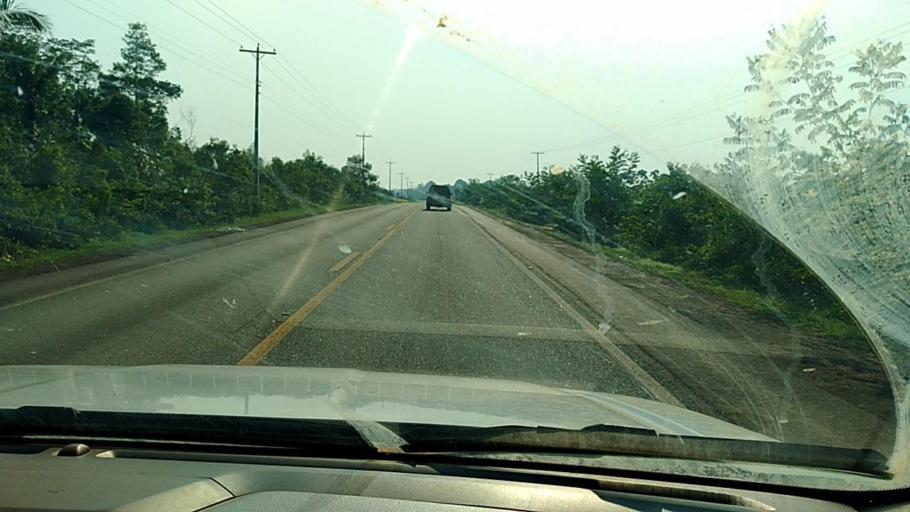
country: BR
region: Rondonia
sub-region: Porto Velho
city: Porto Velho
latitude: -8.2025
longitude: -63.8762
